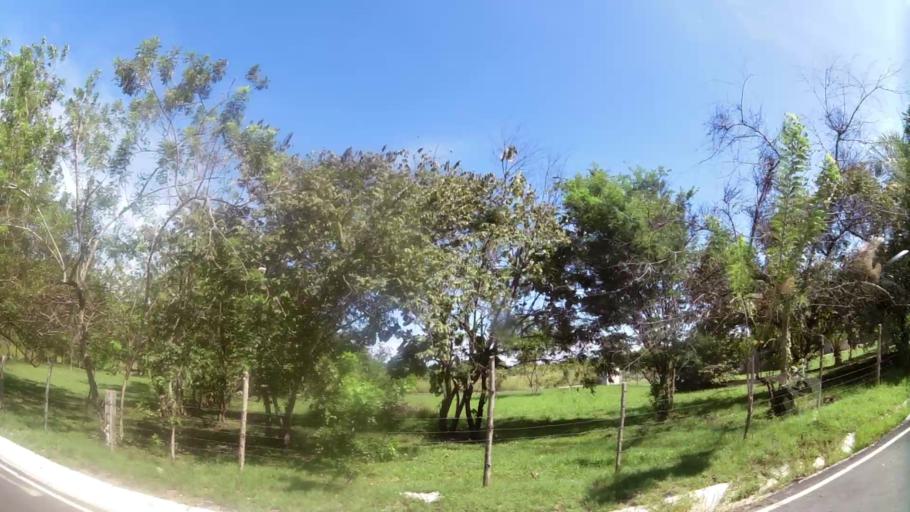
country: PA
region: Panama
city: Nueva Gorgona
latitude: 8.5625
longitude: -79.8750
